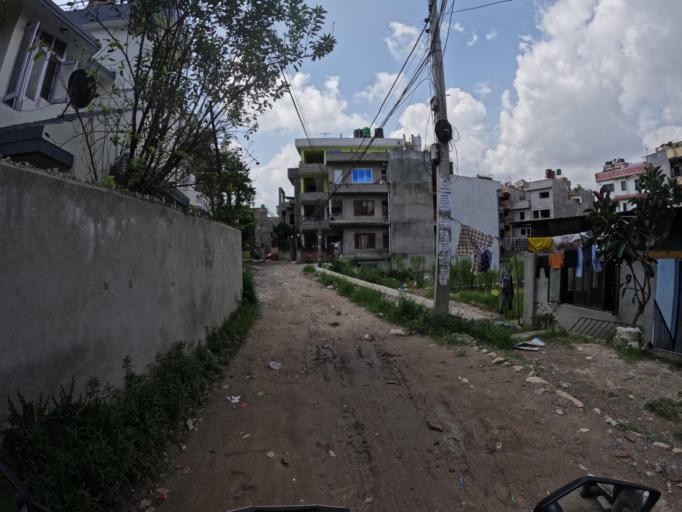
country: NP
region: Central Region
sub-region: Bagmati Zone
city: Patan
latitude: 27.6732
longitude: 85.3618
